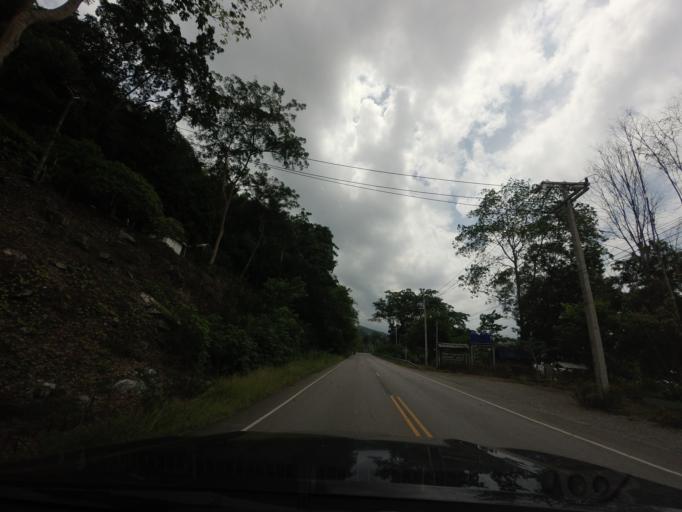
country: TH
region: Loei
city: Pak Chom
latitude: 18.0553
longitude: 101.7762
